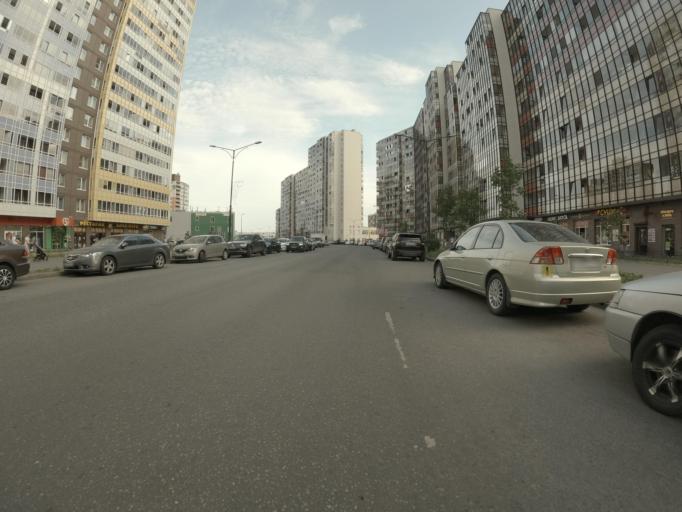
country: RU
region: Leningrad
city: Rybatskoye
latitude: 59.8997
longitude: 30.5117
